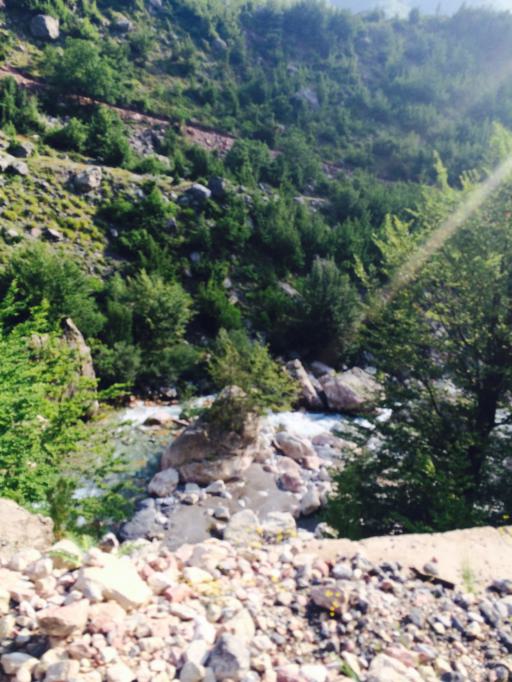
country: AL
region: Shkoder
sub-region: Rrethi i Shkodres
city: Nicaj-Shale
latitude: 42.3844
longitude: 19.7828
